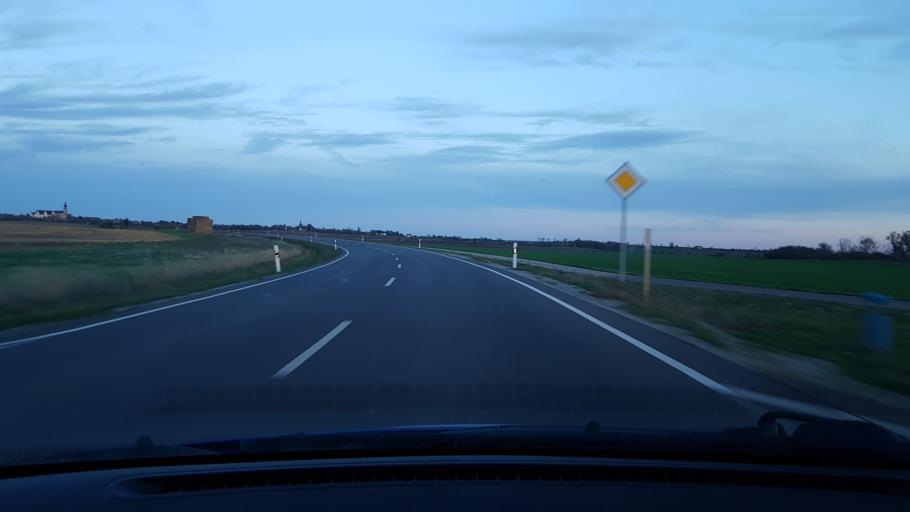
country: DE
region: Saxony-Anhalt
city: Leitzkau
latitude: 52.0603
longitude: 11.9191
